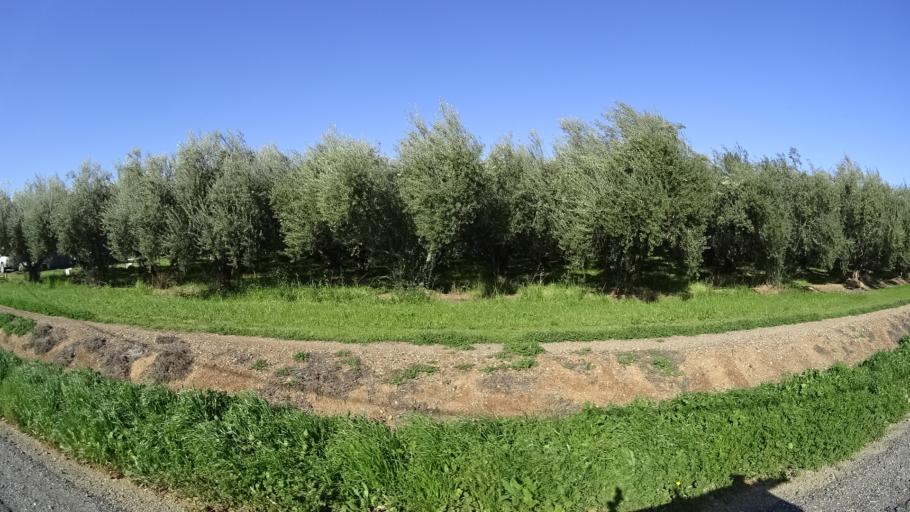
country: US
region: California
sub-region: Glenn County
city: Hamilton City
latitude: 39.7692
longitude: -122.0854
